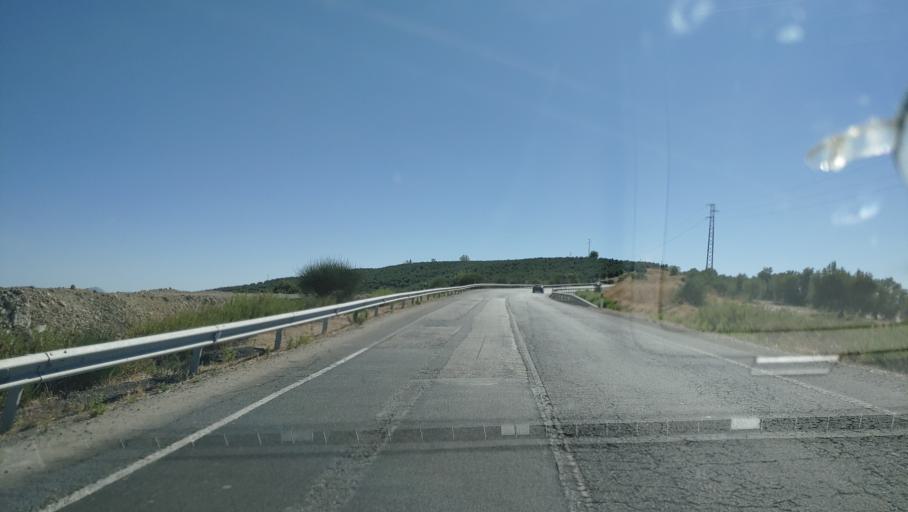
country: ES
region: Andalusia
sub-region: Provincia de Jaen
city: Iznatoraf
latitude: 38.1363
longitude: -3.0502
